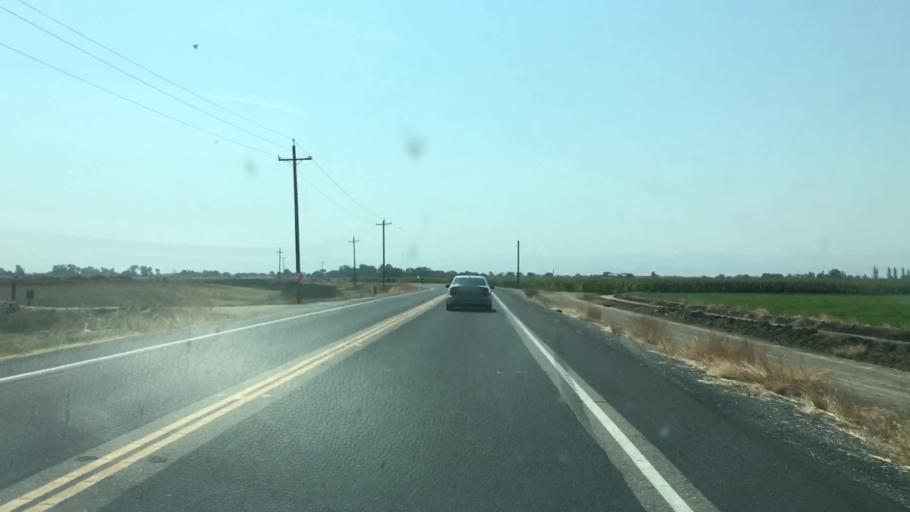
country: US
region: California
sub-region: San Joaquin County
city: Tracy
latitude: 37.8359
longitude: -121.4513
